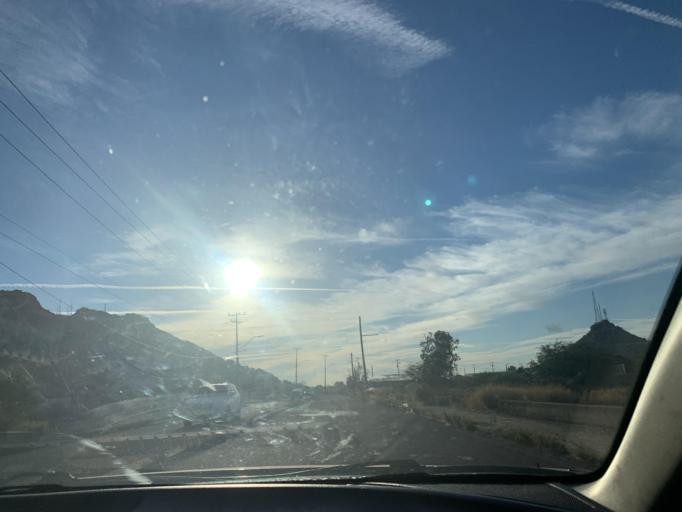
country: MX
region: Sonora
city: Hermosillo
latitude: 29.0727
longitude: -110.9316
